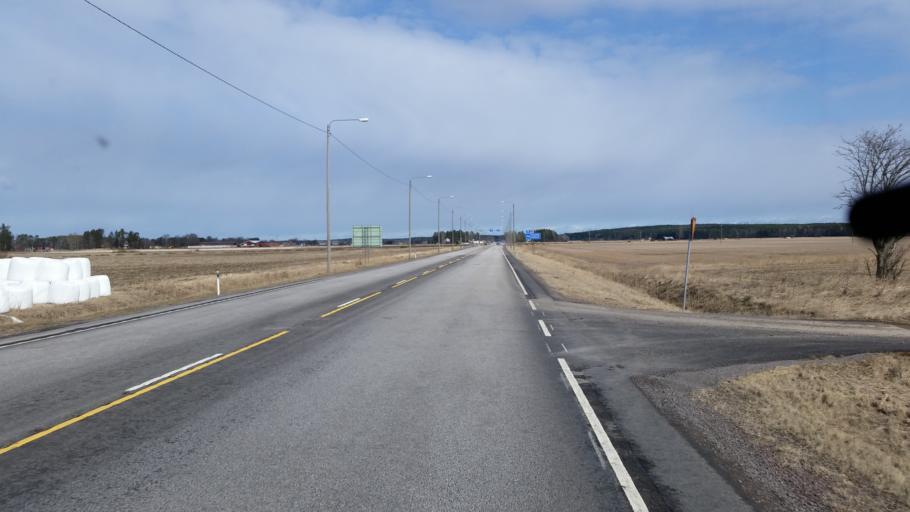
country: FI
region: Uusimaa
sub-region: Loviisa
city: Lapinjaervi
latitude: 60.6520
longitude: 26.2381
